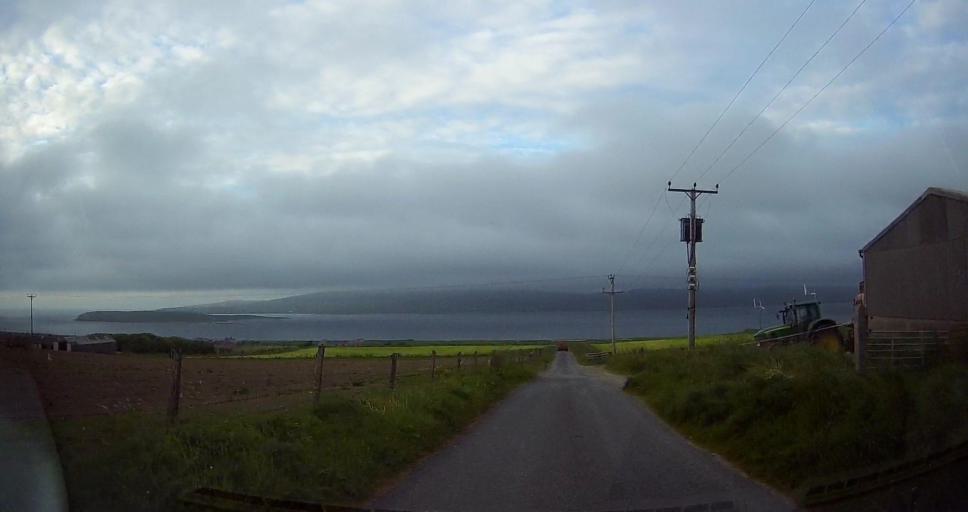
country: GB
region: Scotland
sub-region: Orkney Islands
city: Orkney
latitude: 59.1186
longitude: -3.1291
